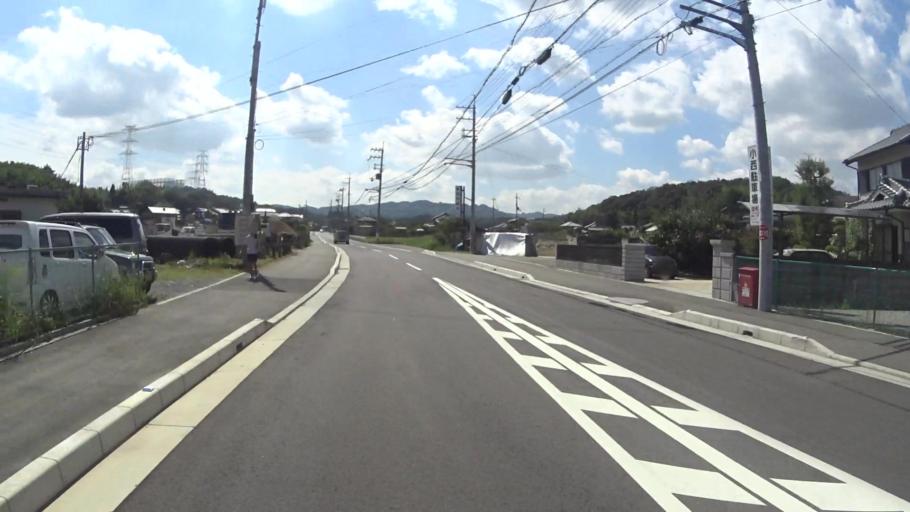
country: JP
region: Kyoto
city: Tanabe
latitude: 34.7985
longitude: 135.7738
